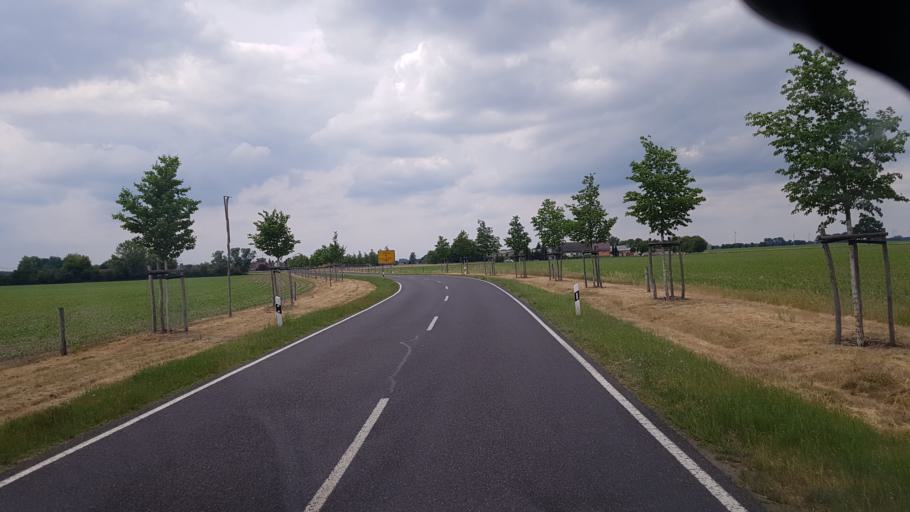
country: DE
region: Brandenburg
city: Ihlow
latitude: 51.8454
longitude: 13.2553
